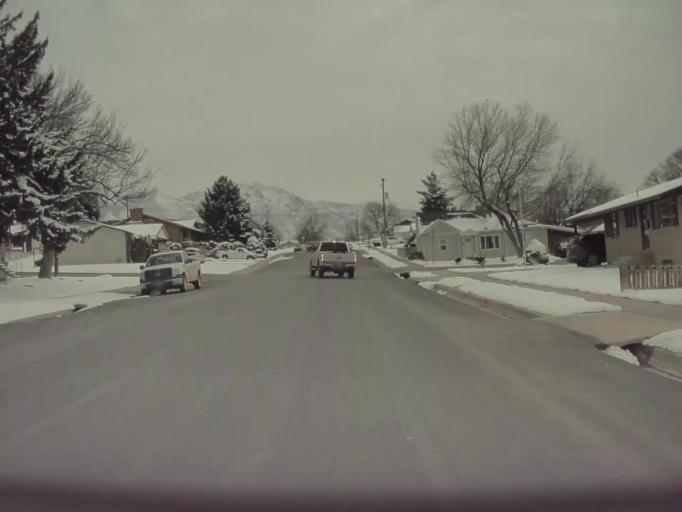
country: US
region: Utah
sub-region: Utah County
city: Spanish Fork
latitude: 40.1130
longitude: -111.6390
